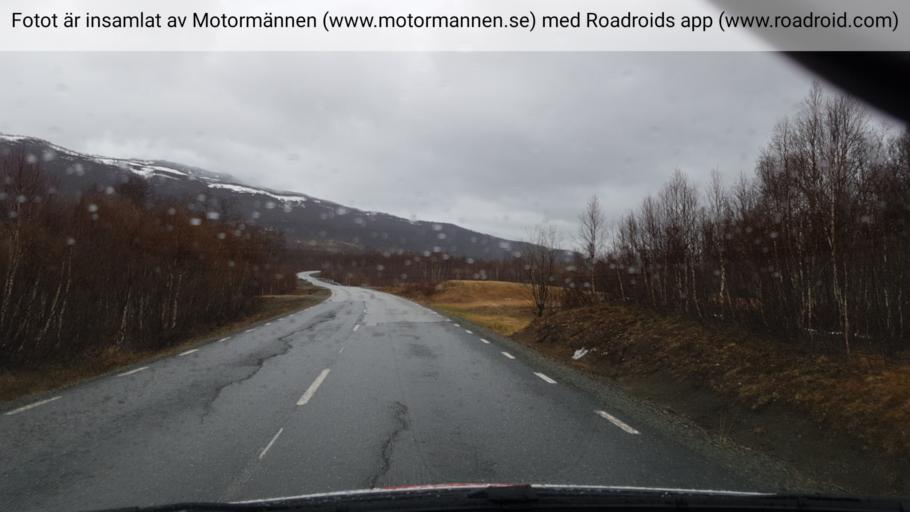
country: NO
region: Nordland
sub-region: Rana
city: Mo i Rana
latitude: 65.7819
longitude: 15.1199
